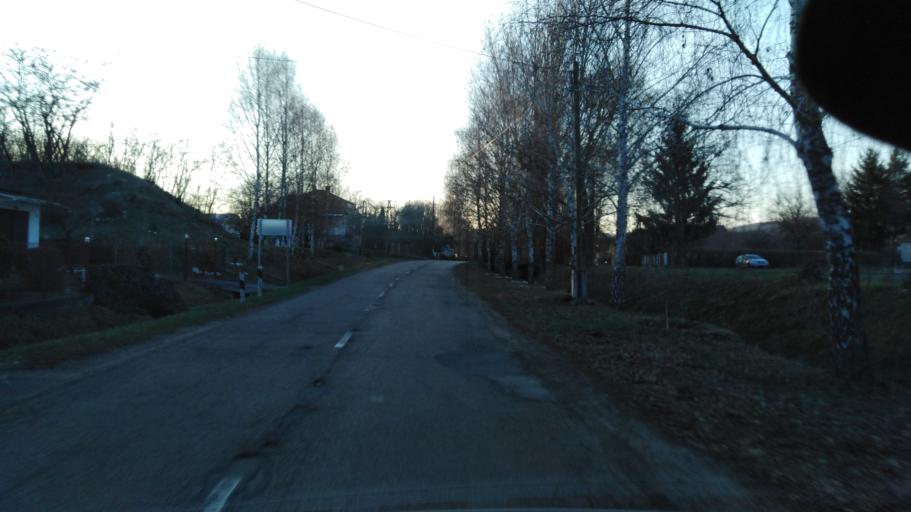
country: HU
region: Nograd
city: Kazar
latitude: 48.0494
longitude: 19.8510
